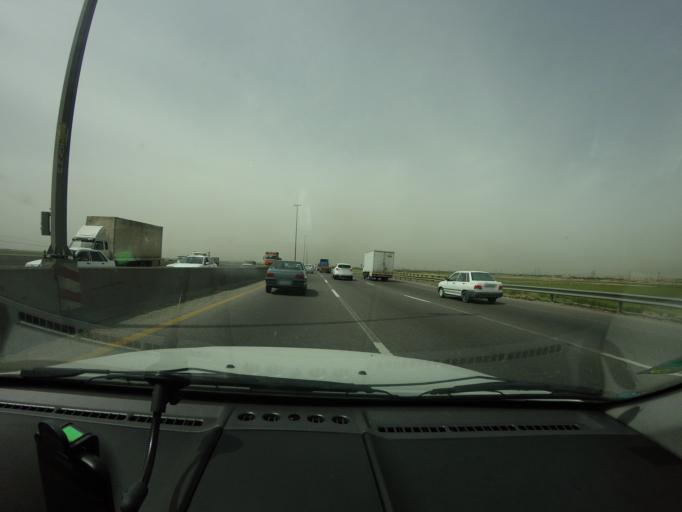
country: IR
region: Tehran
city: Eslamshahr
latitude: 35.6023
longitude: 51.1908
